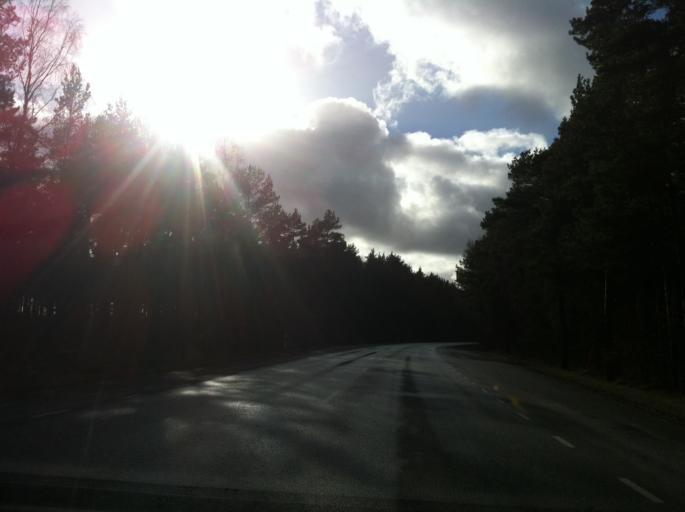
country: SE
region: Skane
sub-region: Bromolla Kommun
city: Bromoella
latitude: 56.0558
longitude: 14.4826
